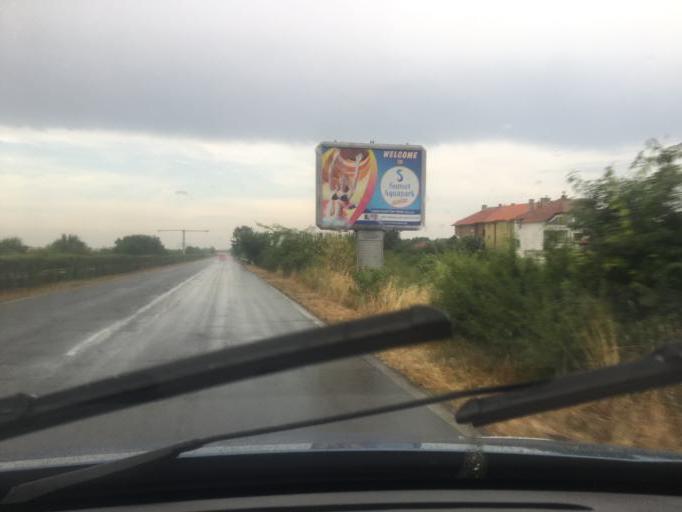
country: BG
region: Burgas
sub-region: Obshtina Burgas
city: Burgas
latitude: 42.5655
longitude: 27.5287
